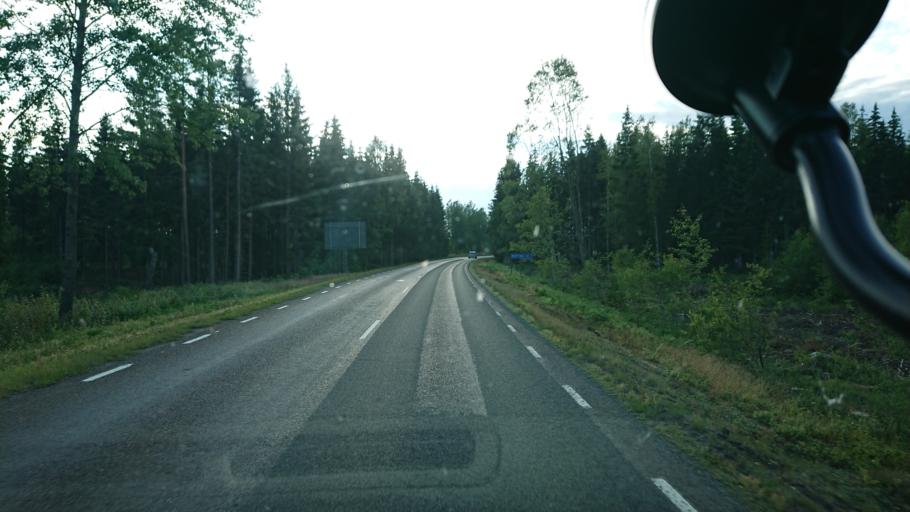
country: SE
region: Kronoberg
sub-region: Vaxjo Kommun
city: Braas
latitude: 57.0177
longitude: 15.0493
